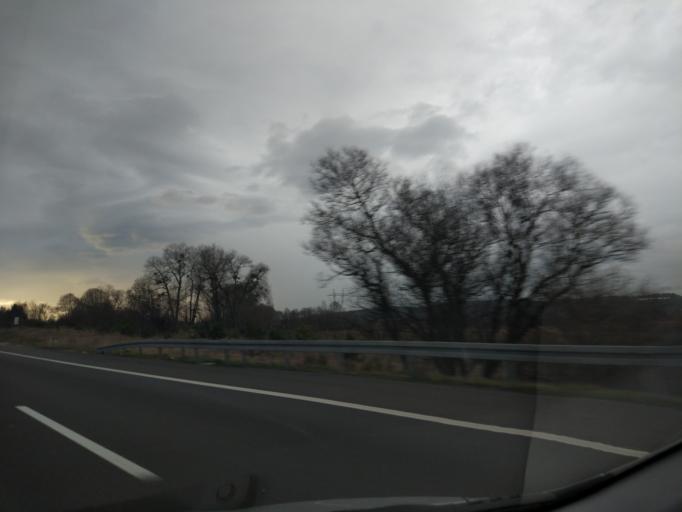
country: TR
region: Bolu
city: Yenicaga
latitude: 40.7518
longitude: 31.9415
